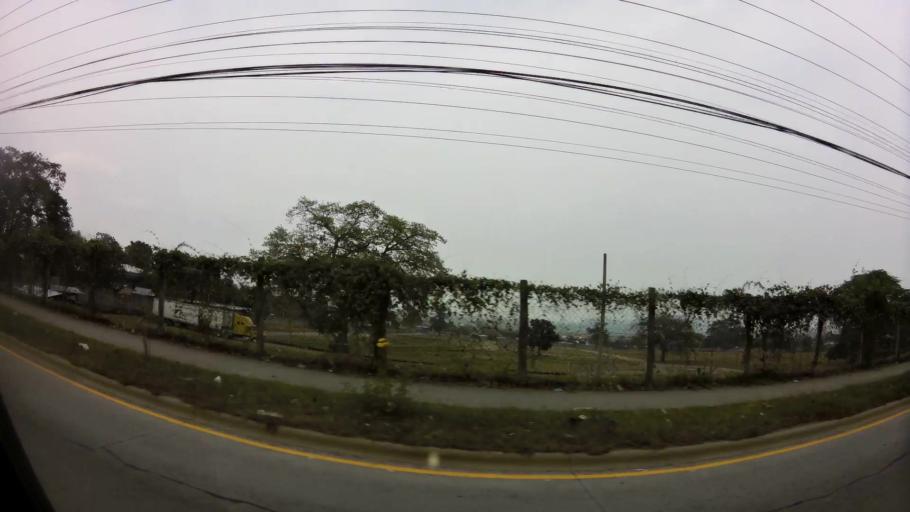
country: HN
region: Cortes
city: Armenta
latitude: 15.4669
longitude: -88.0331
